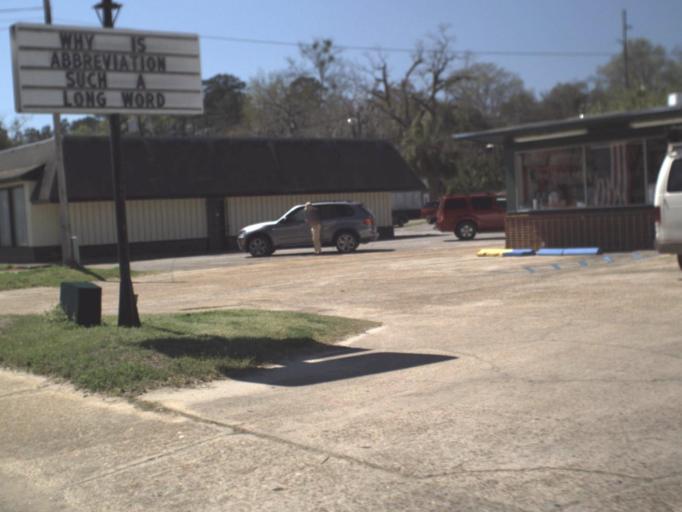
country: US
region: Florida
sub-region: Leon County
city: Tallahassee
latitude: 30.4291
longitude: -84.2807
